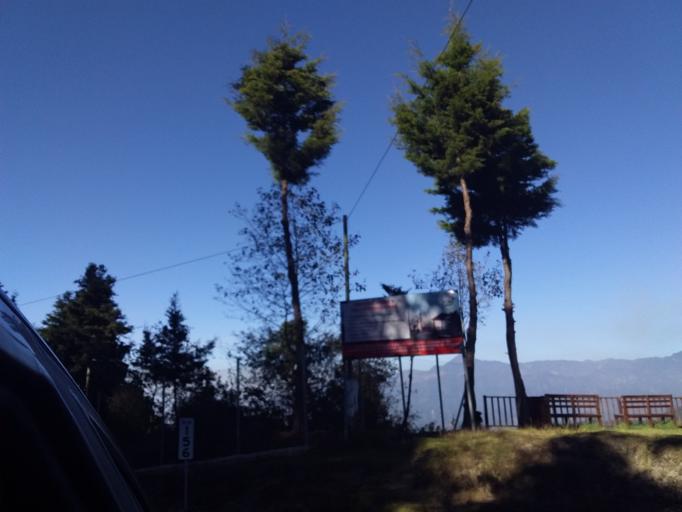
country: GT
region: Solola
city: Santa Lucia Utatlan
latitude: 14.7547
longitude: -91.3021
